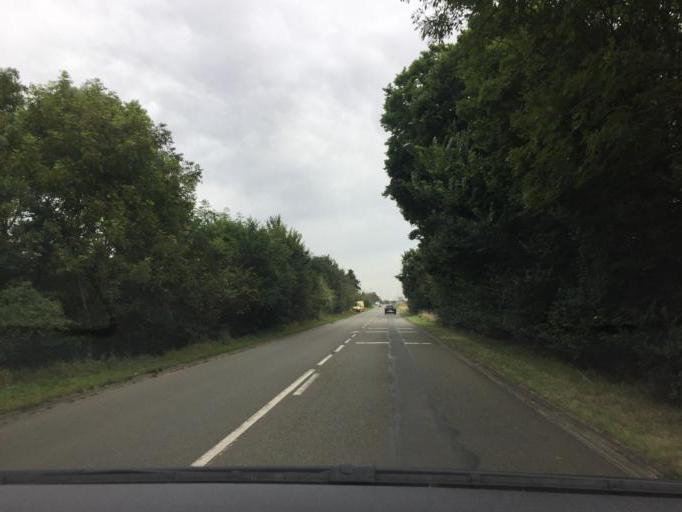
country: FR
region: Ile-de-France
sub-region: Departement des Yvelines
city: Les Loges-en-Josas
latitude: 48.7566
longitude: 2.1217
